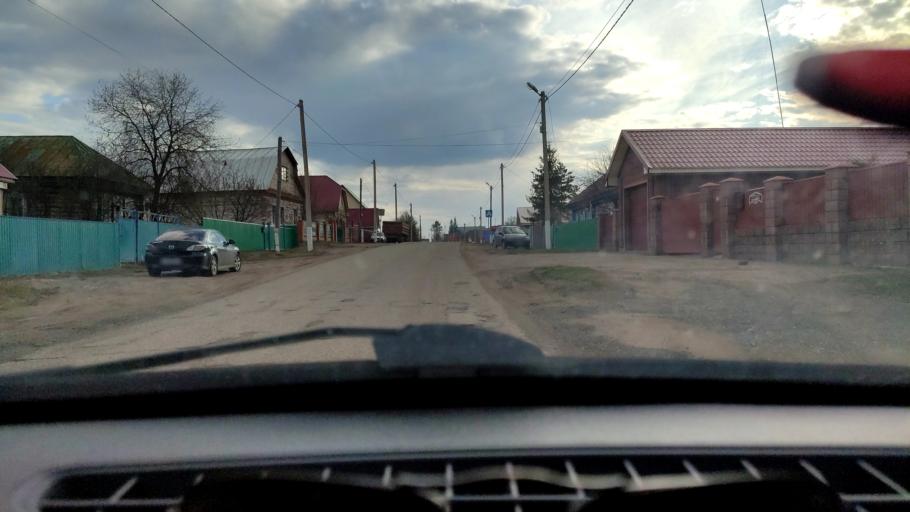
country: RU
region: Bashkortostan
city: Karmaskaly
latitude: 54.3694
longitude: 56.1871
